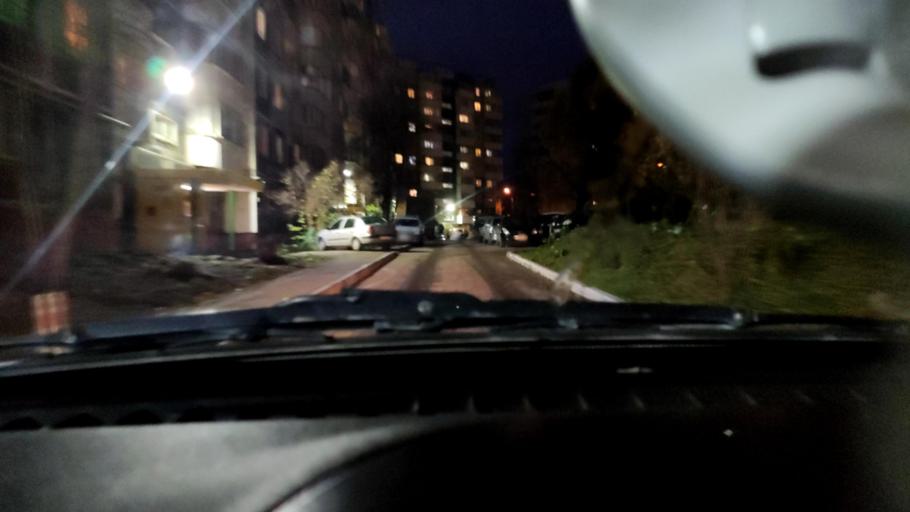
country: RU
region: Perm
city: Perm
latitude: 58.0107
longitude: 56.3122
